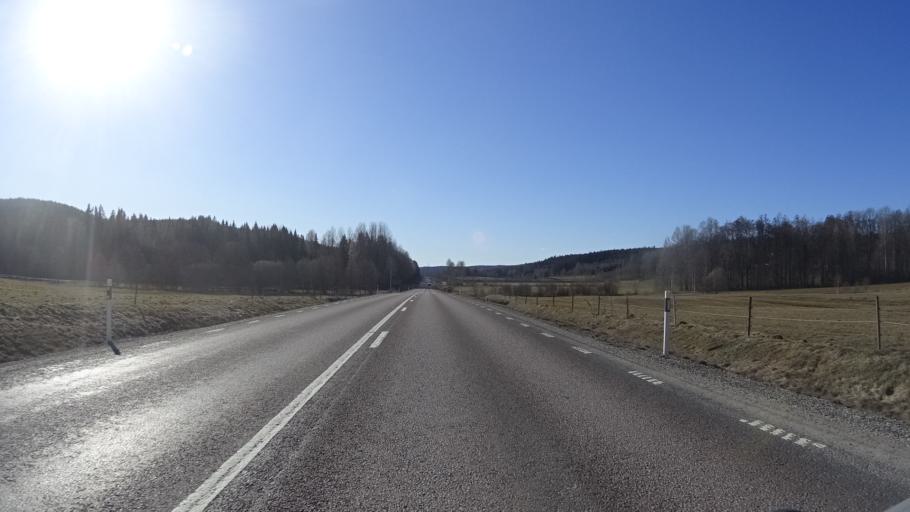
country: SE
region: Vaermland
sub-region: Arvika Kommun
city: Arvika
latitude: 59.6673
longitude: 12.8388
